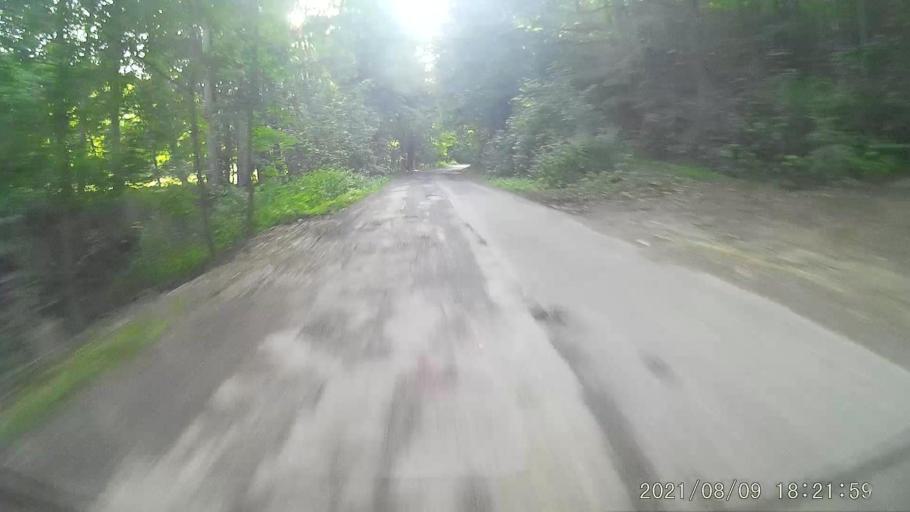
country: PL
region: Lower Silesian Voivodeship
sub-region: Powiat zabkowicki
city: Bardo
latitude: 50.5066
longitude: 16.7057
